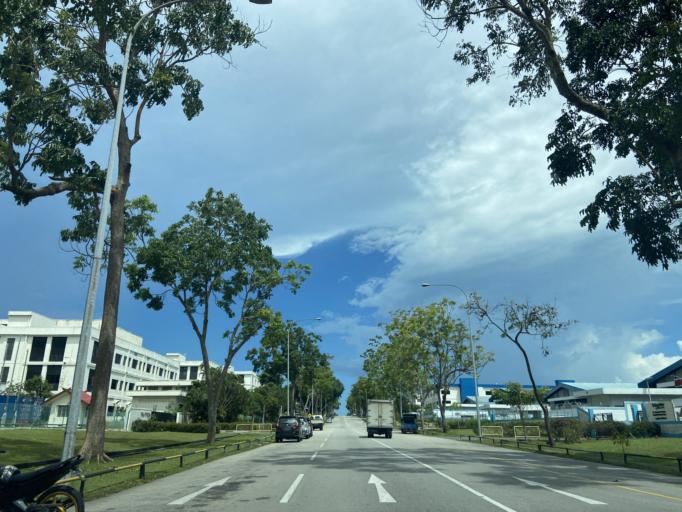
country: SG
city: Singapore
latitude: 1.0673
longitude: 104.0272
